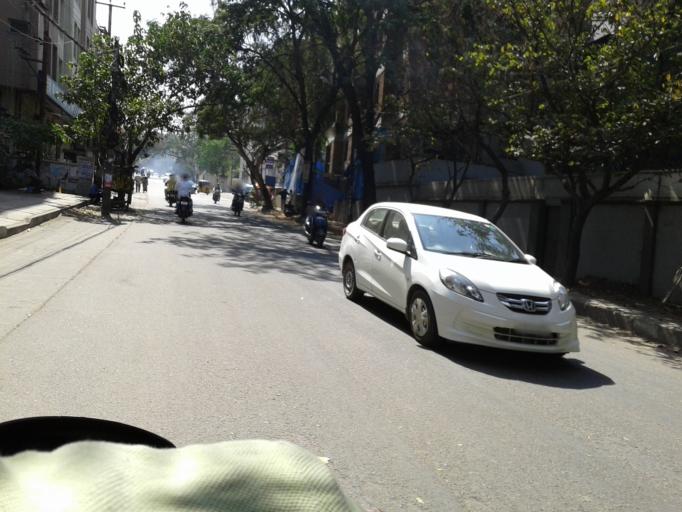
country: IN
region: Telangana
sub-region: Hyderabad
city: Hyderabad
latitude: 17.4294
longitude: 78.4395
